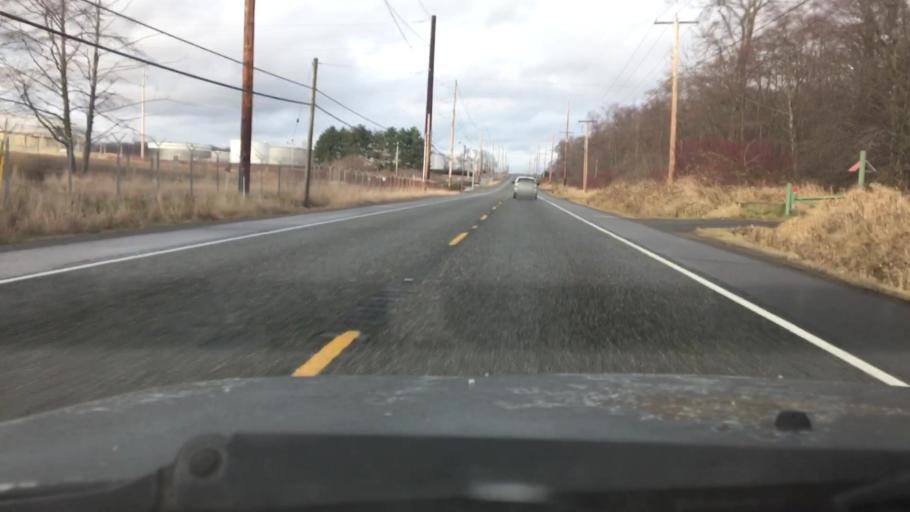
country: US
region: Washington
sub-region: Whatcom County
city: Ferndale
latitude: 48.8268
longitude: -122.6825
